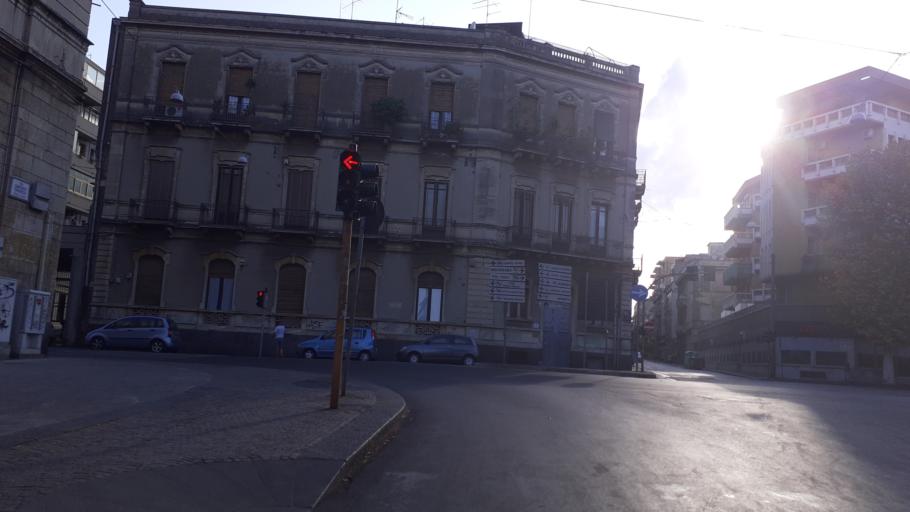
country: IT
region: Sicily
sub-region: Catania
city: Catania
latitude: 37.5089
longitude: 15.0830
